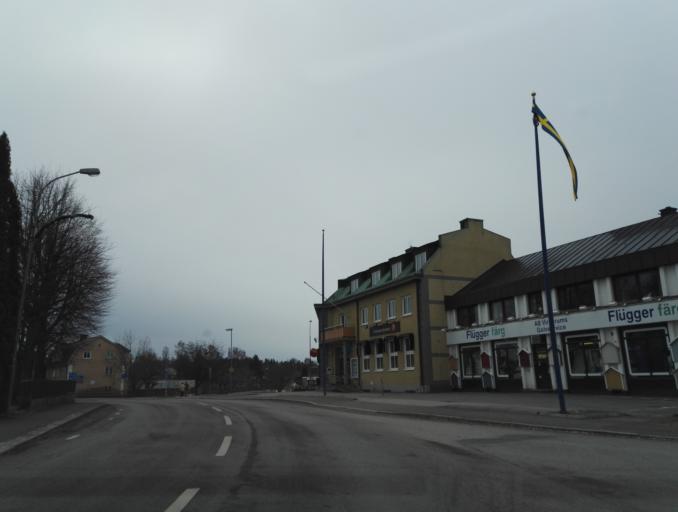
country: SE
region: Kalmar
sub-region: Hultsfreds Kommun
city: Virserum
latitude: 57.3200
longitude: 15.5812
